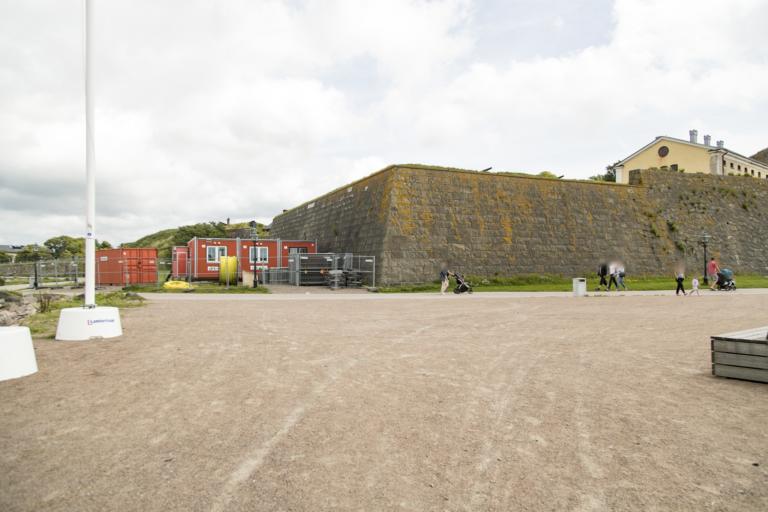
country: SE
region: Halland
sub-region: Varbergs Kommun
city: Varberg
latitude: 57.1075
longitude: 12.2385
